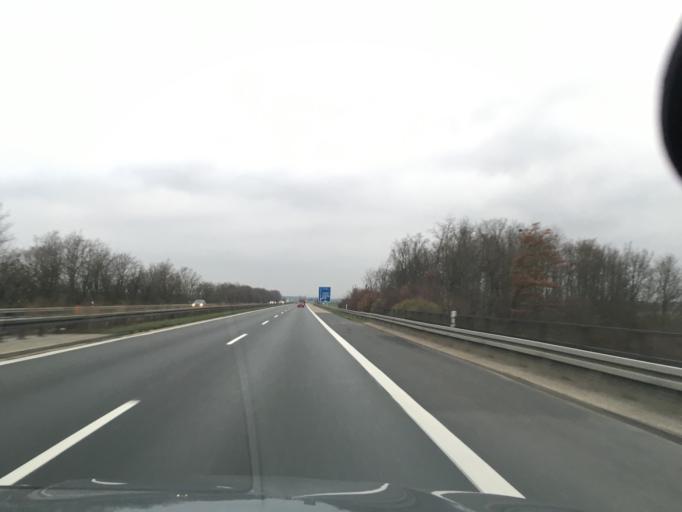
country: DE
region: Bavaria
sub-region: Regierungsbezirk Unterfranken
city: Wiesentheid
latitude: 49.7743
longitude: 10.3648
